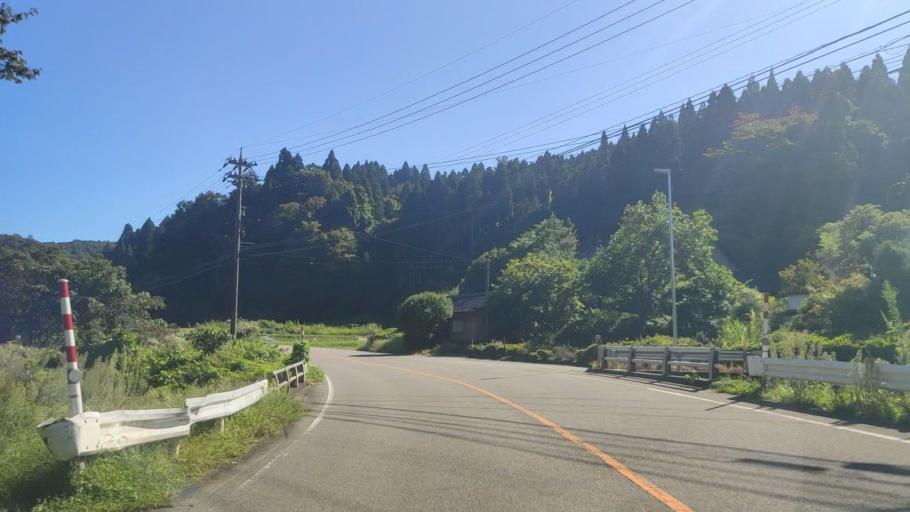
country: JP
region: Ishikawa
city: Nanao
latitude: 37.3334
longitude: 137.2074
